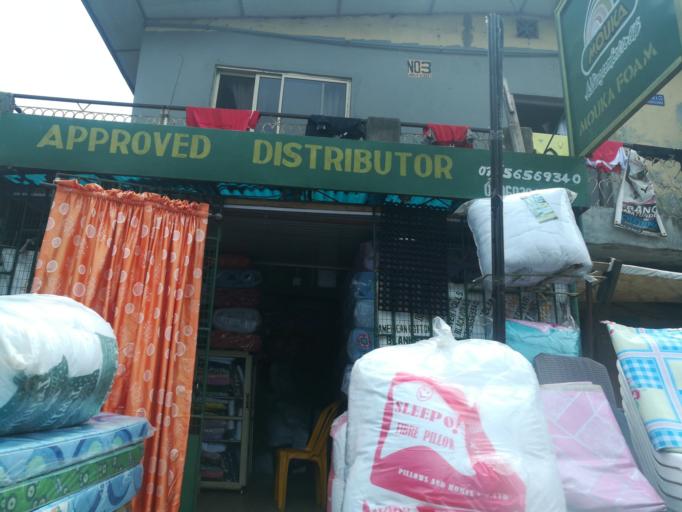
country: NG
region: Lagos
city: Ojota
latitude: 6.5714
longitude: 3.3625
